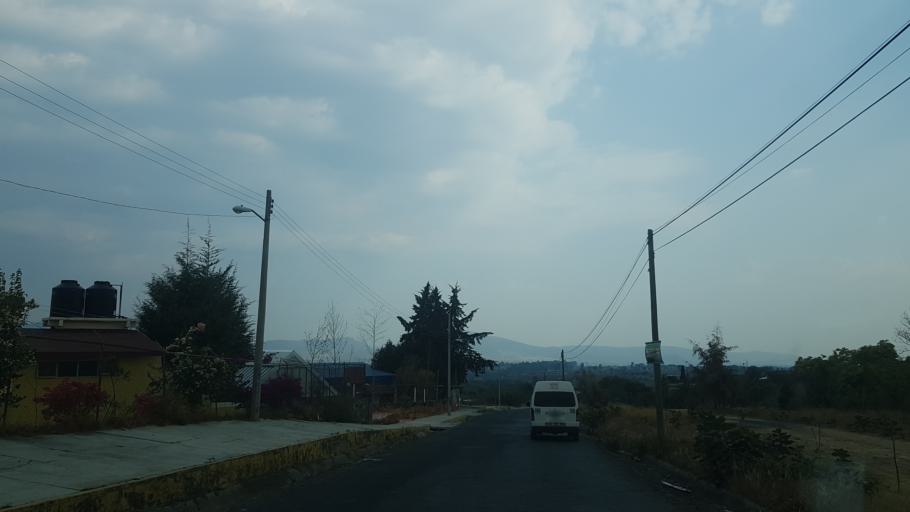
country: MX
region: Puebla
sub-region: Santa Isabel Cholula
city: San Martin Tlamapa
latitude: 18.9729
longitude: -98.3945
